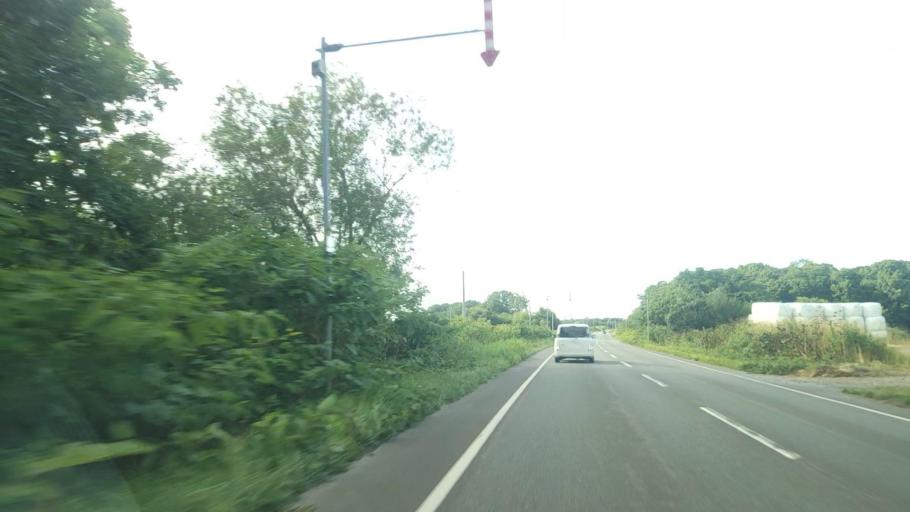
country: JP
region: Hokkaido
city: Makubetsu
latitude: 45.0535
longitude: 141.7498
